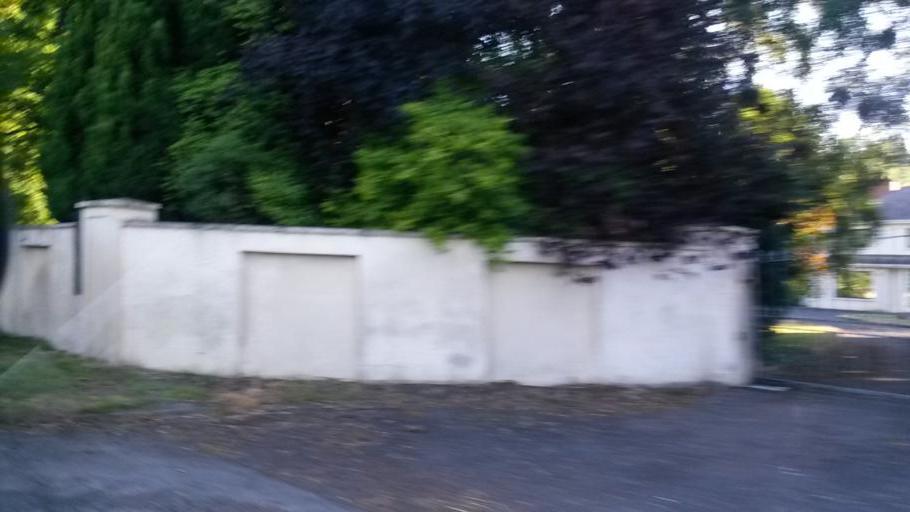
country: IE
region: Leinster
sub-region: An Mhi
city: Ashbourne
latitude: 53.5039
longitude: -6.3443
